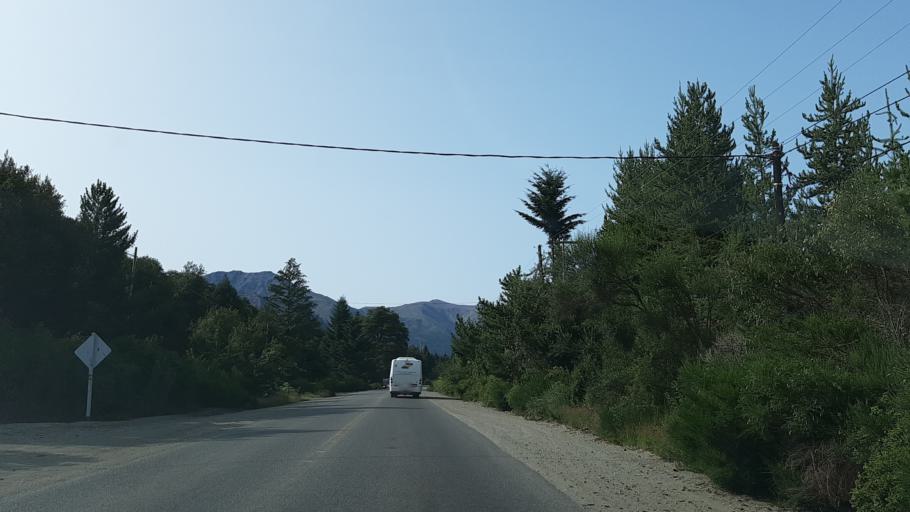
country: AR
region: Rio Negro
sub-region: Departamento de Bariloche
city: San Carlos de Bariloche
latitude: -41.1486
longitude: -71.4094
